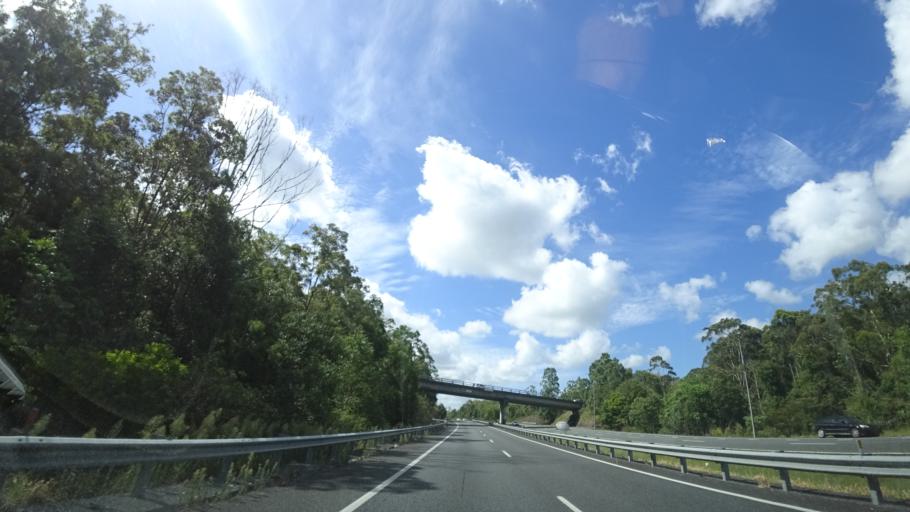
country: AU
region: Queensland
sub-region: Sunshine Coast
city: Twin Waters
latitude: -26.5971
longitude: 152.9716
